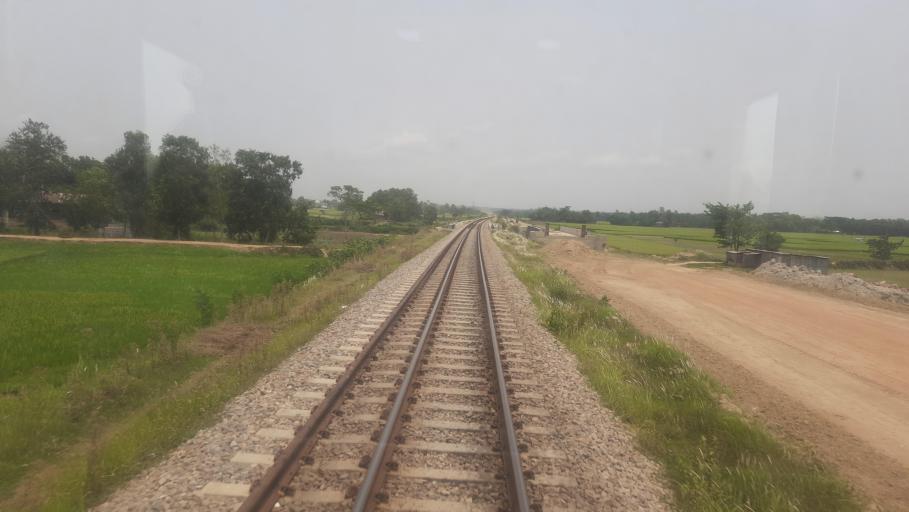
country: BD
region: Chittagong
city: Comilla
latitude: 23.6527
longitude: 91.1495
